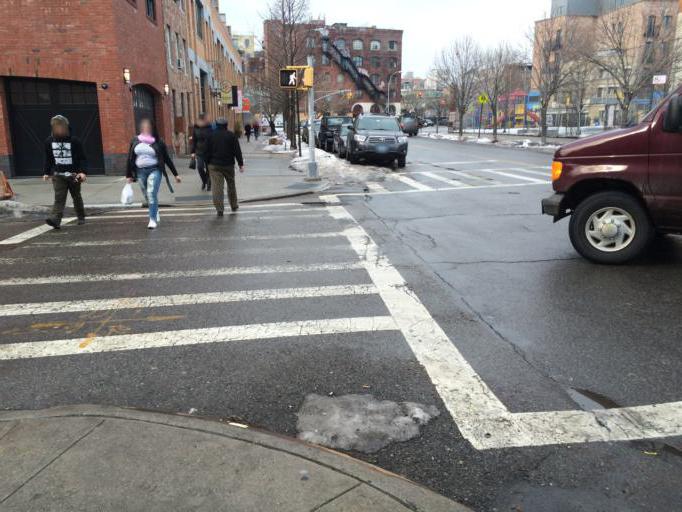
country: US
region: New York
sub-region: Queens County
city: Long Island City
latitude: 40.7152
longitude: -73.9562
